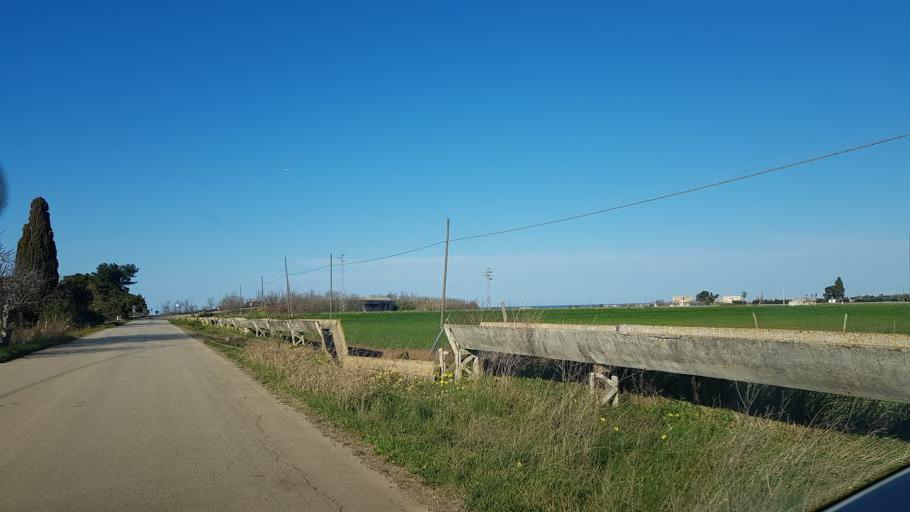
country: IT
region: Apulia
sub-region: Provincia di Brindisi
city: San Vito dei Normanni
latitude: 40.6862
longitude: 17.8224
